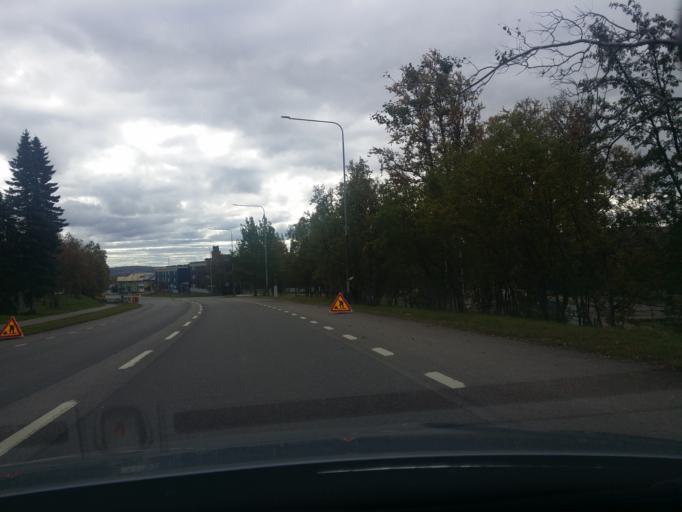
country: SE
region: Norrbotten
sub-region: Kiruna Kommun
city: Kiruna
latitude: 67.8502
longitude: 20.2248
